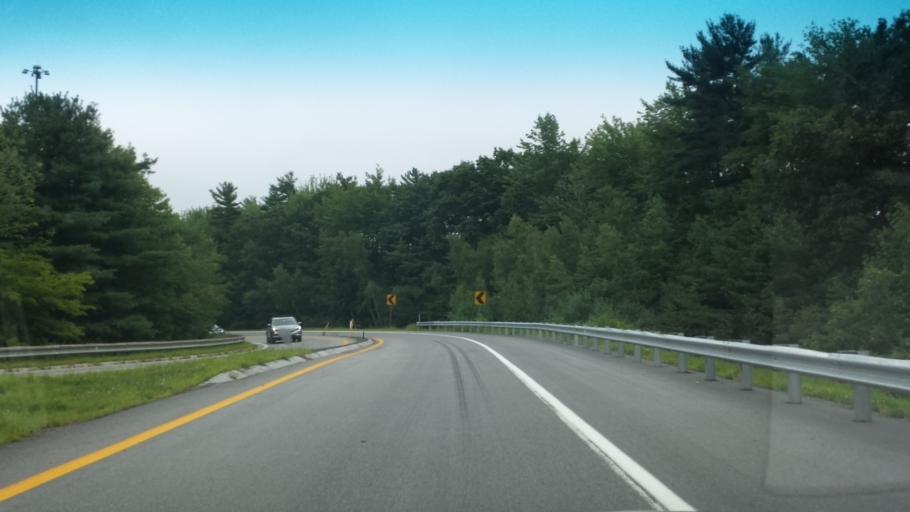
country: US
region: Maine
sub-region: Cumberland County
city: South Portland Gardens
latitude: 43.6255
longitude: -70.3301
